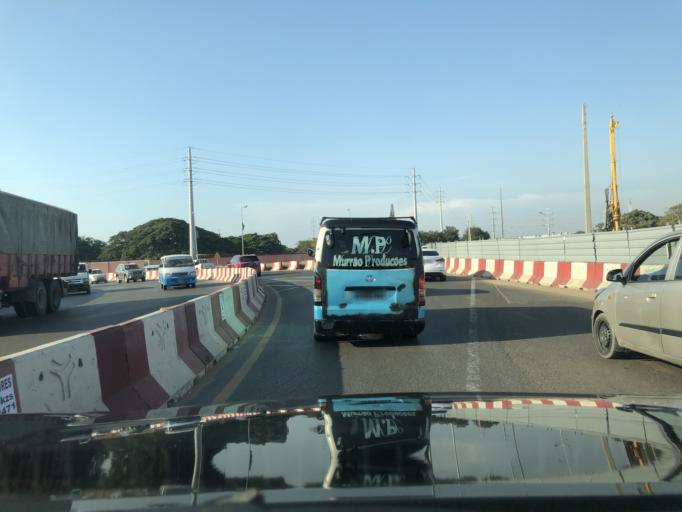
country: AO
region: Luanda
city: Luanda
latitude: -8.9087
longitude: 13.1800
